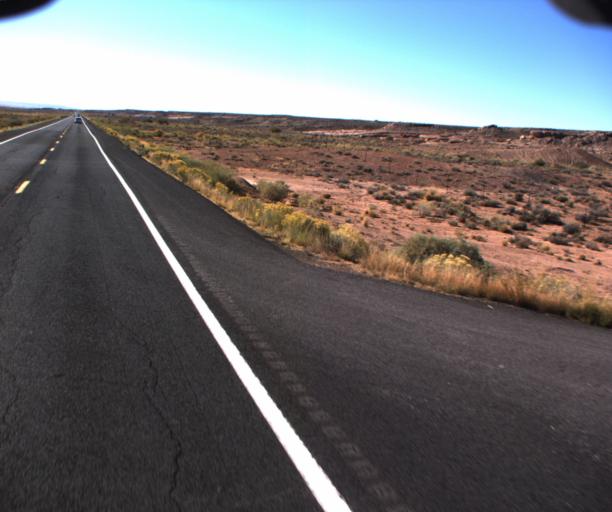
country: US
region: Arizona
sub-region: Coconino County
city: Tuba City
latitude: 36.1729
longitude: -111.3995
